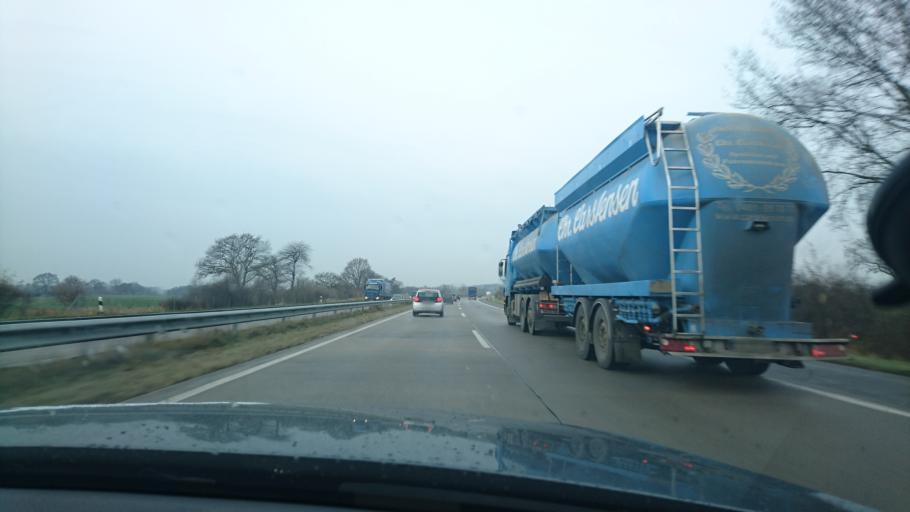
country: DE
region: Schleswig-Holstein
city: Ratekau
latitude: 53.9660
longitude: 10.7366
